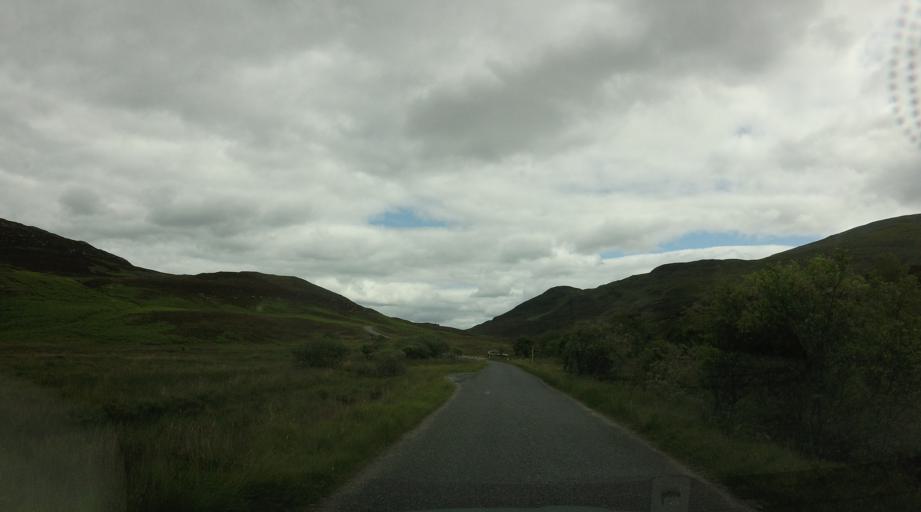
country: GB
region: Scotland
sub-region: Perth and Kinross
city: Aberfeldy
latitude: 56.6880
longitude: -4.0933
